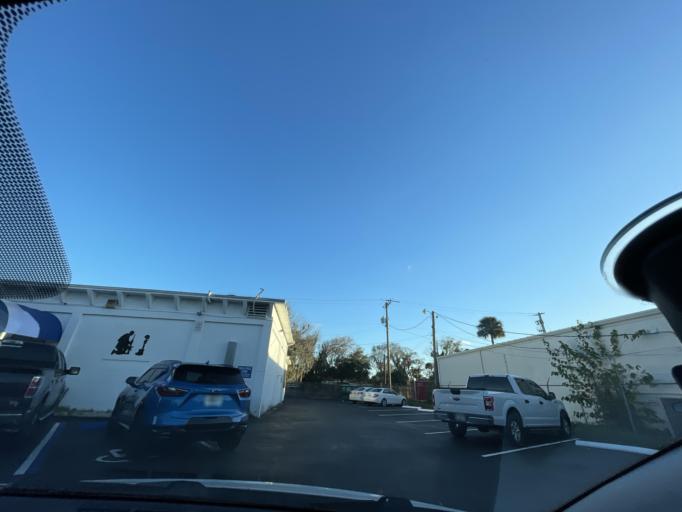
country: US
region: Florida
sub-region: Volusia County
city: Daytona Beach
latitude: 29.2182
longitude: -81.0479
